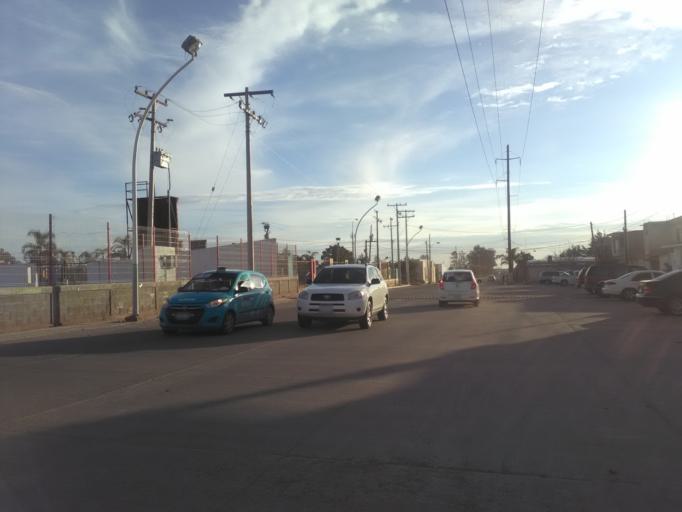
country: MX
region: Durango
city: Victoria de Durango
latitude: 24.0469
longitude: -104.6626
